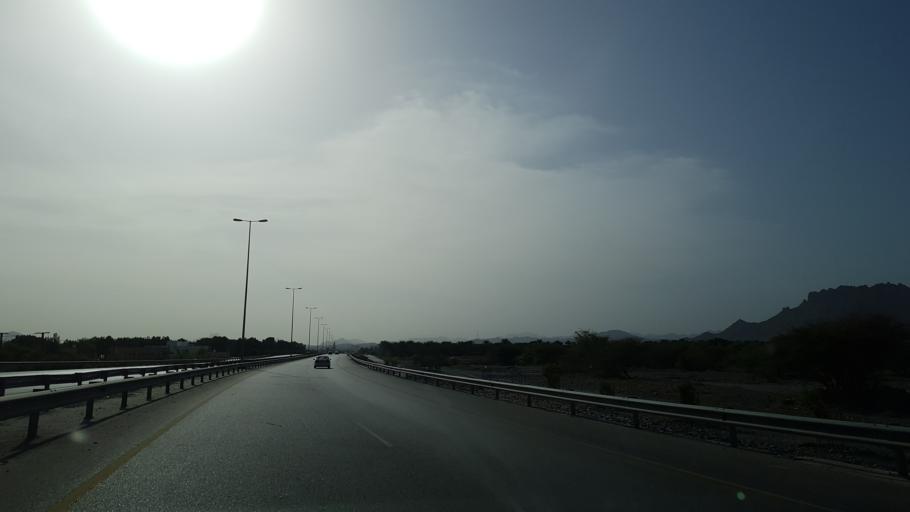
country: OM
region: Muhafazat ad Dakhiliyah
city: Nizwa
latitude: 22.8579
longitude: 57.5669
